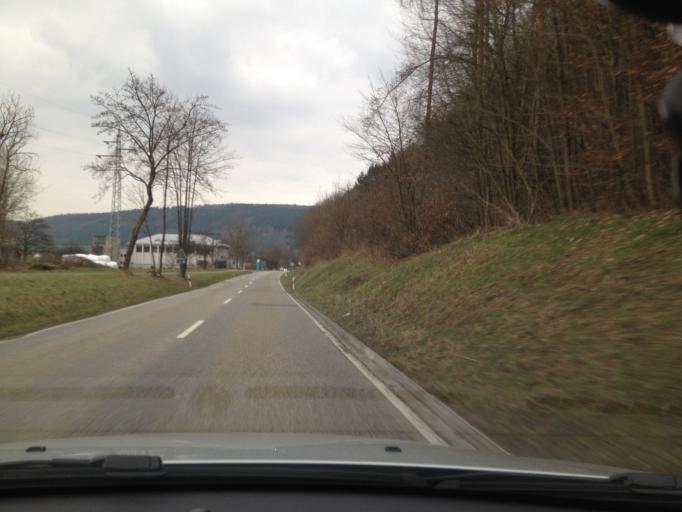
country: DE
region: Bavaria
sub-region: Regierungsbezirk Unterfranken
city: Faulbach
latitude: 49.7818
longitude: 9.4367
